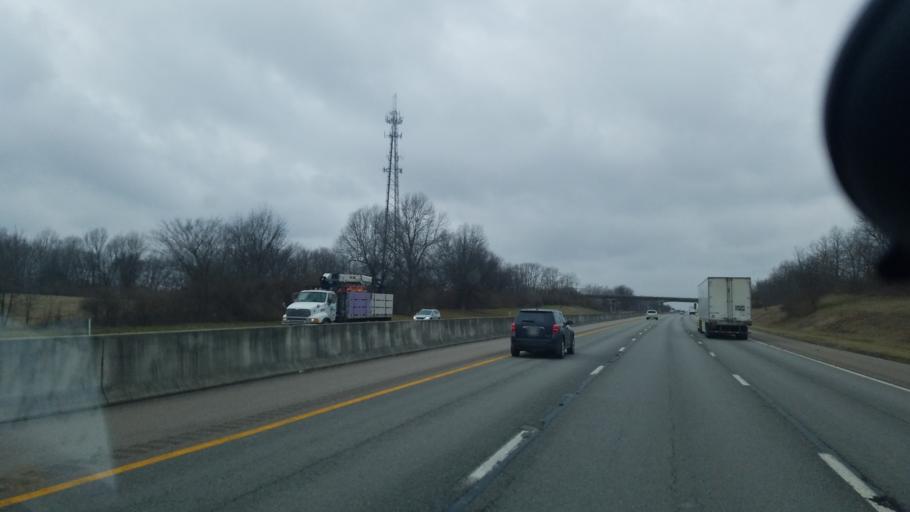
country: US
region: Kentucky
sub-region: Fayette County
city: Lexington-Fayette
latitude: 38.0513
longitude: -84.3494
